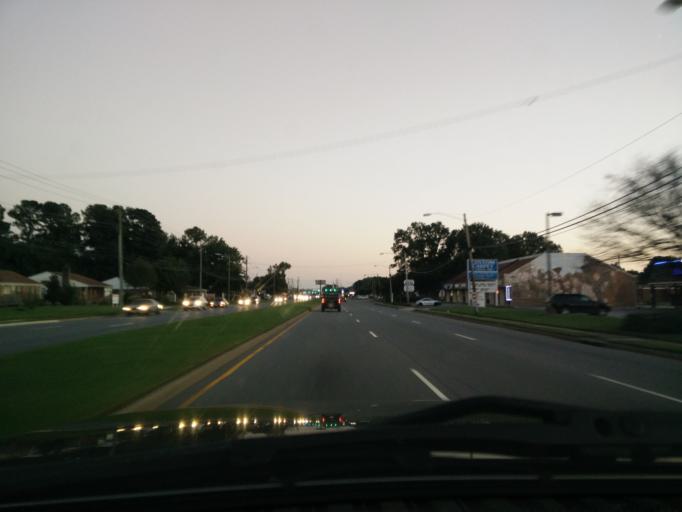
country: US
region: Virginia
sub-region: City of Chesapeake
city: Chesapeake
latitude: 36.7612
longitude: -76.2506
